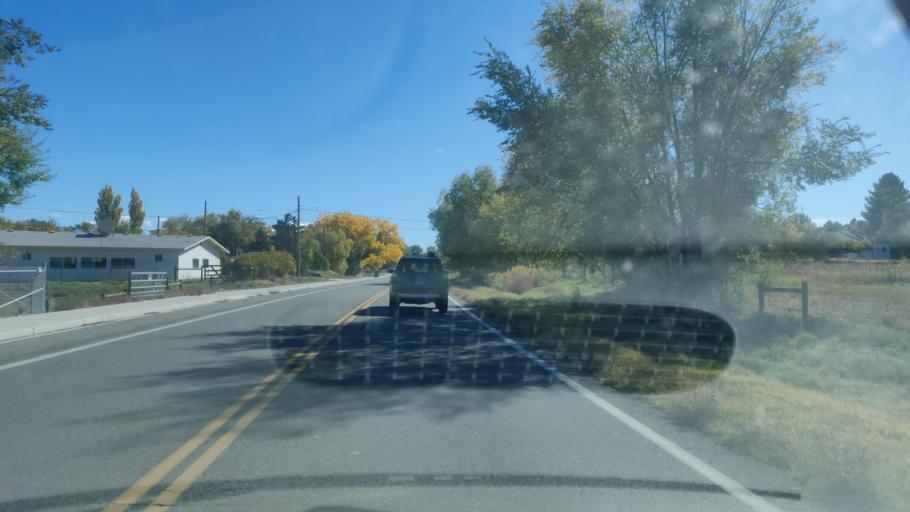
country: US
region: Colorado
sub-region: Mesa County
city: Redlands
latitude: 39.0735
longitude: -108.6226
